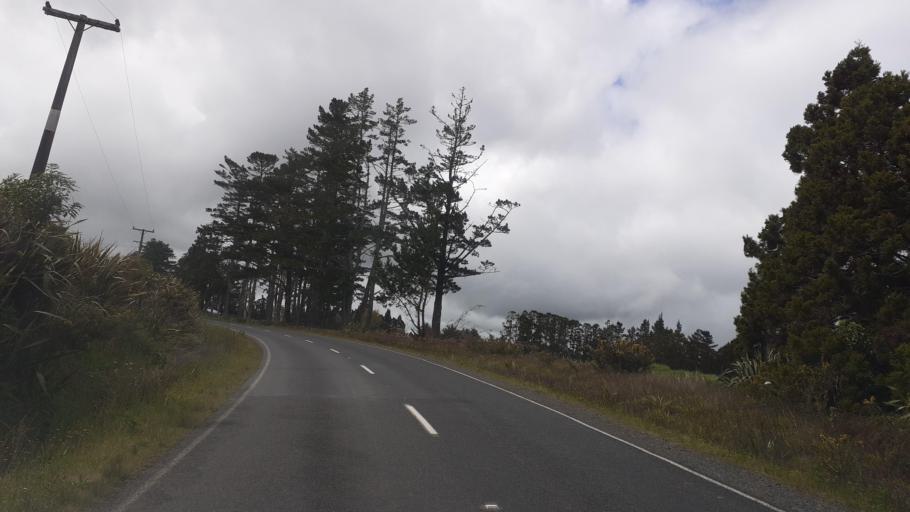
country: NZ
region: Northland
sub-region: Far North District
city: Waimate North
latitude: -35.2560
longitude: 173.7994
